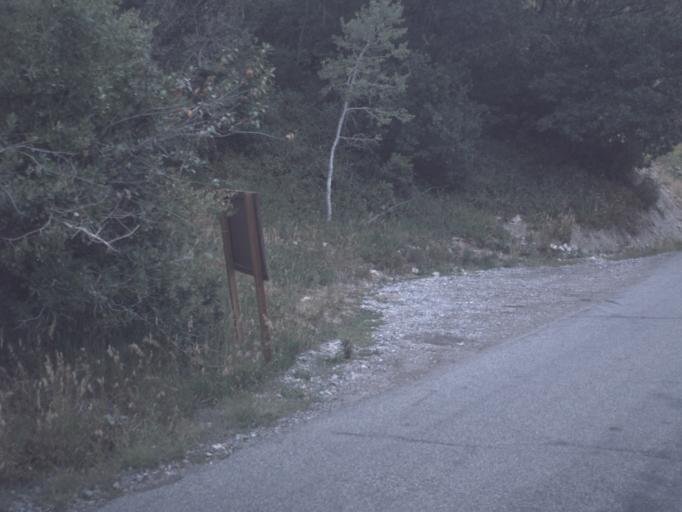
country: US
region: Utah
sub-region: Utah County
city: Lindon
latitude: 40.3929
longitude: -111.5807
